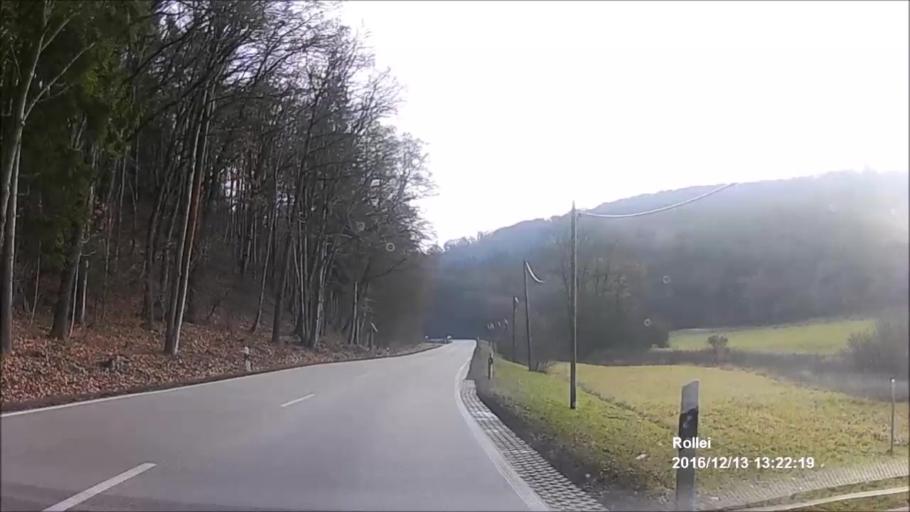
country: DE
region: Thuringia
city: Nauendorf
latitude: 50.9020
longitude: 11.1700
